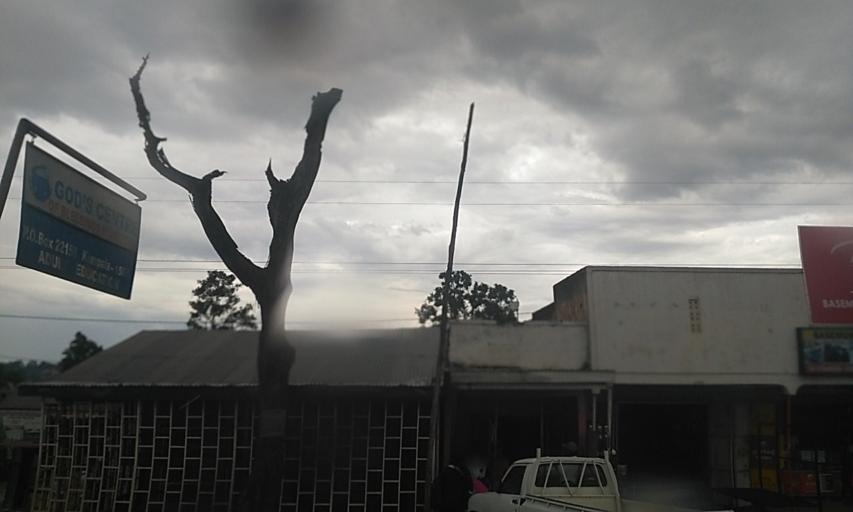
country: UG
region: Central Region
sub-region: Wakiso District
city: Bweyogerere
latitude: 0.3529
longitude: 32.6607
